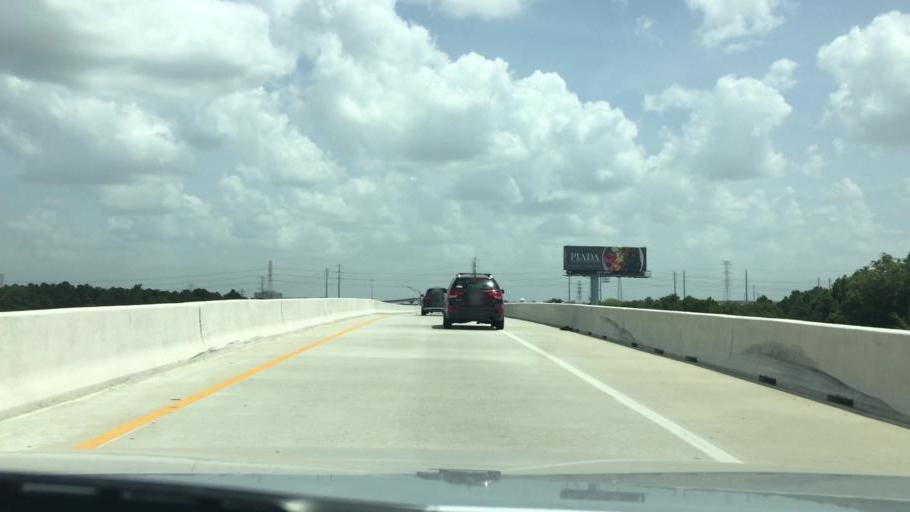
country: US
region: Texas
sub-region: Harris County
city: Hudson
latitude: 29.9448
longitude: -95.5268
